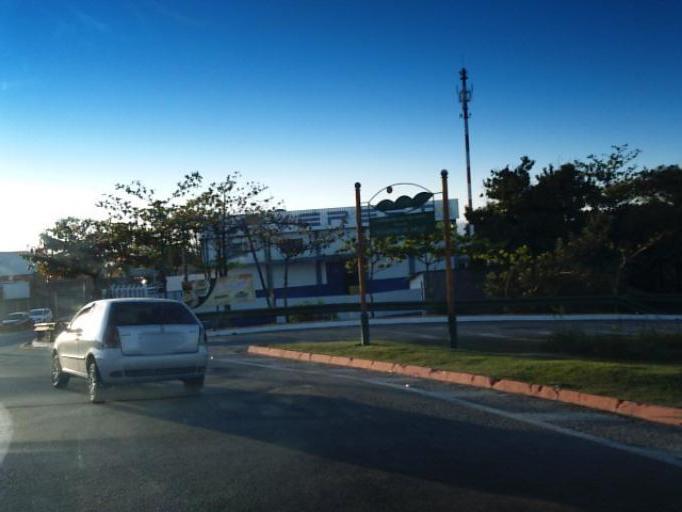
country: BR
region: Sao Paulo
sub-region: Cacapava
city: Cacapava
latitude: -23.1480
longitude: -45.7793
